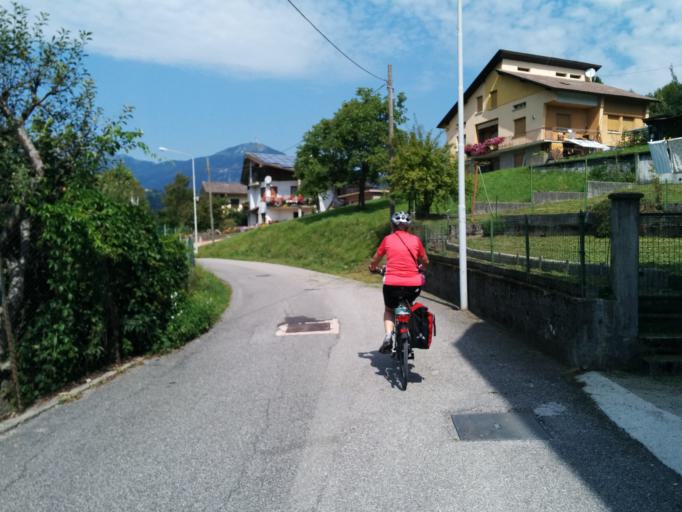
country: IT
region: Friuli Venezia Giulia
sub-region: Provincia di Udine
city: Ovaro
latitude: 46.4814
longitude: 12.8680
